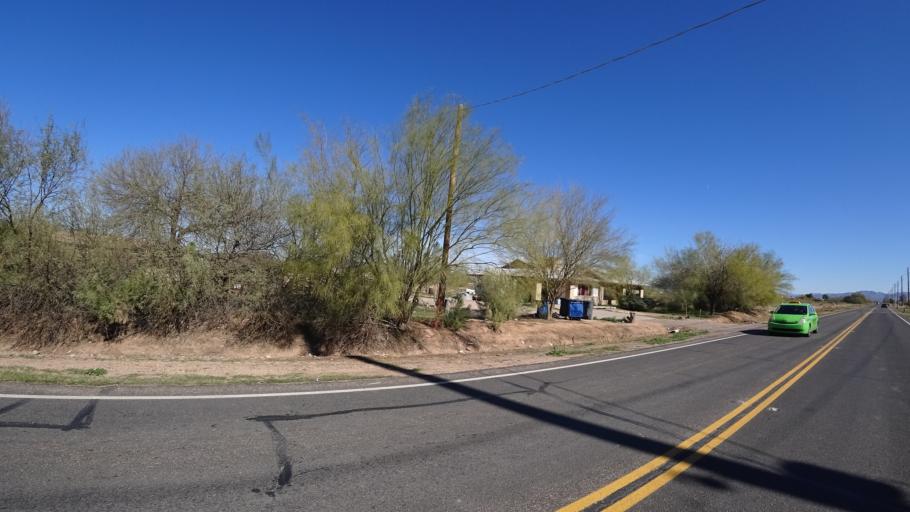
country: US
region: Arizona
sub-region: Maricopa County
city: Scottsdale
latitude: 33.4951
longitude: -111.8563
